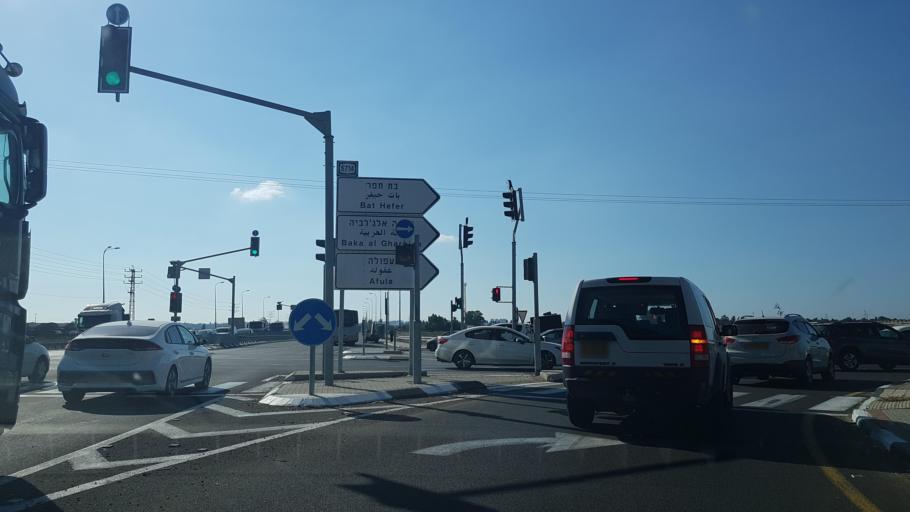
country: PS
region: West Bank
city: Tulkarm
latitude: 32.3120
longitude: 34.9995
